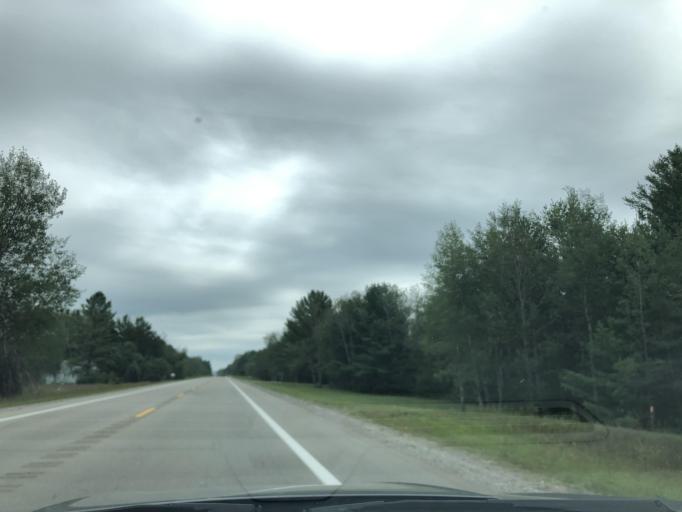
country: US
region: Michigan
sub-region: Clare County
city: Harrison
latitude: 44.0312
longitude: -84.9987
